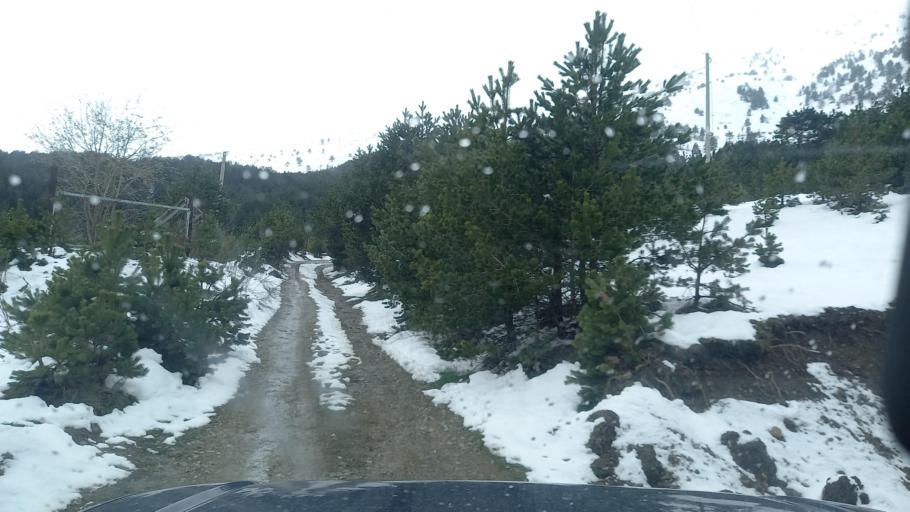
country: RU
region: North Ossetia
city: Mizur
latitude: 42.8100
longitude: 43.9567
